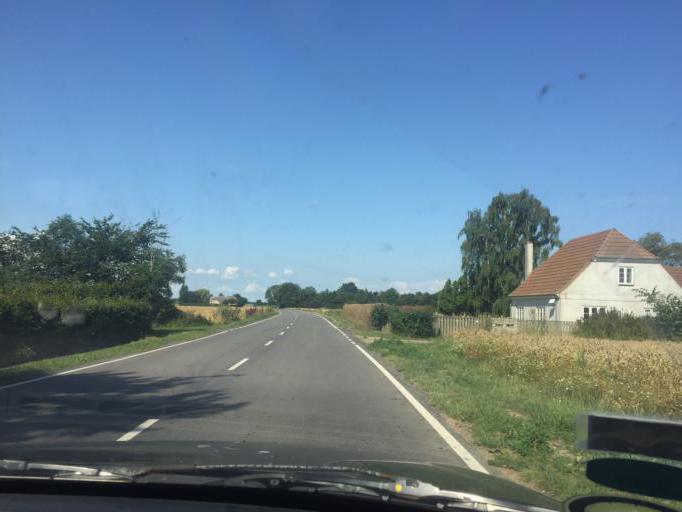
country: DK
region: Zealand
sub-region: Guldborgsund Kommune
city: Sakskobing
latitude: 54.7958
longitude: 11.5621
